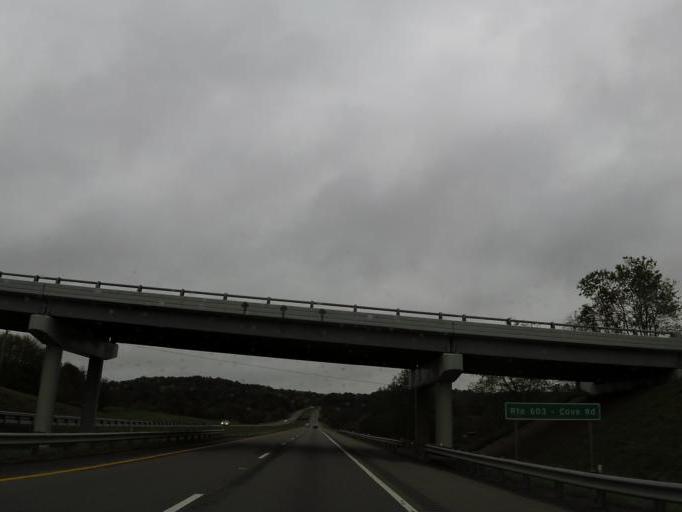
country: US
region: Virginia
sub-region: Wythe County
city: Wytheville
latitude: 36.9872
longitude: -81.0753
